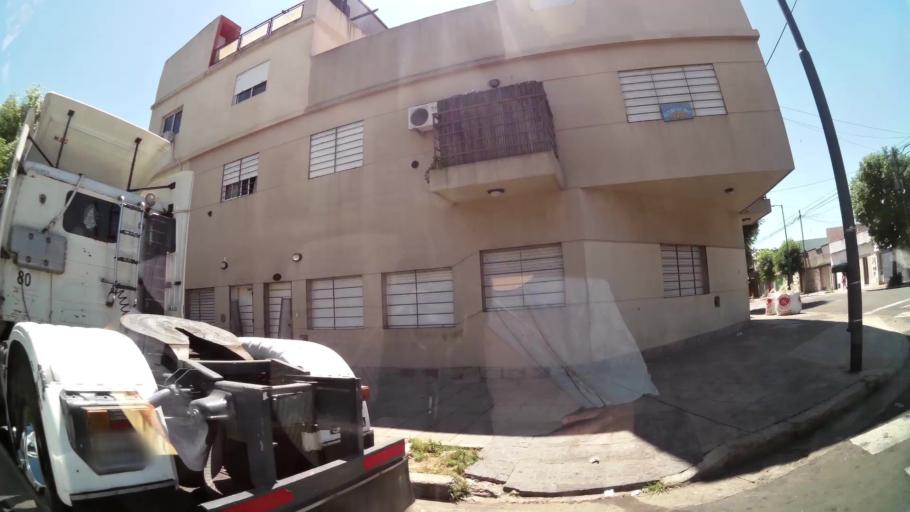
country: AR
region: Buenos Aires
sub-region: Partido de Avellaneda
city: Avellaneda
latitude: -34.6459
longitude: -58.4082
